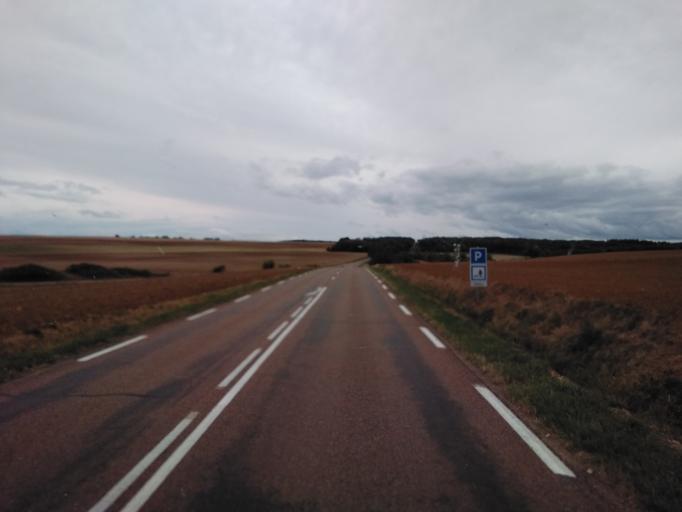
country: FR
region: Champagne-Ardenne
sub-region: Departement de l'Aube
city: Bar-sur-Seine
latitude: 48.1641
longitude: 4.4155
